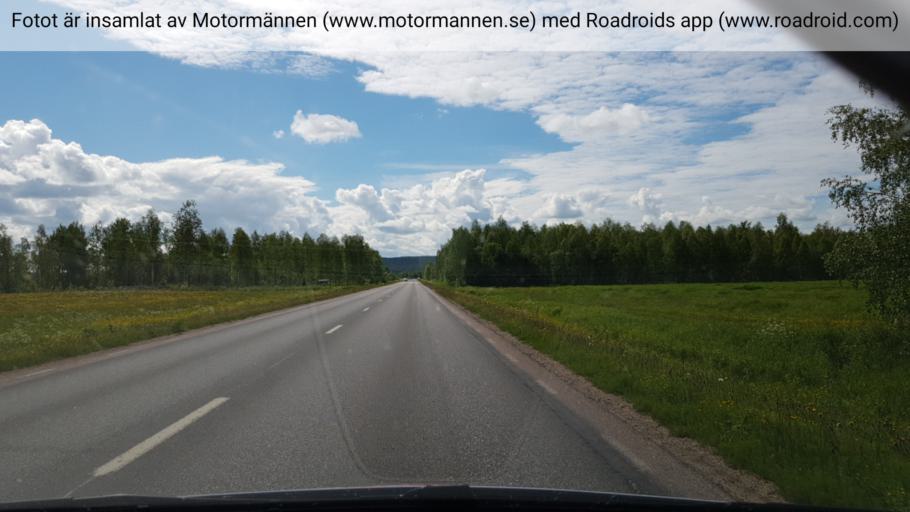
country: SE
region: Norrbotten
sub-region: Overtornea Kommun
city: OEvertornea
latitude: 66.4099
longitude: 23.6239
